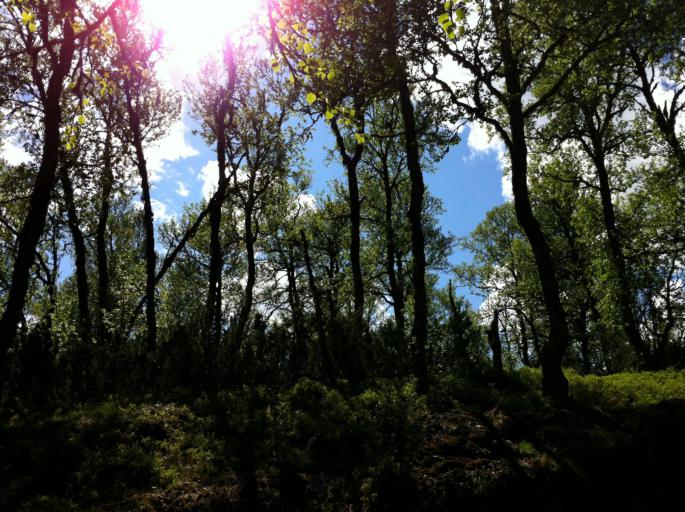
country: NO
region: Sor-Trondelag
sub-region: Tydal
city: Aas
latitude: 62.7065
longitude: 12.4873
